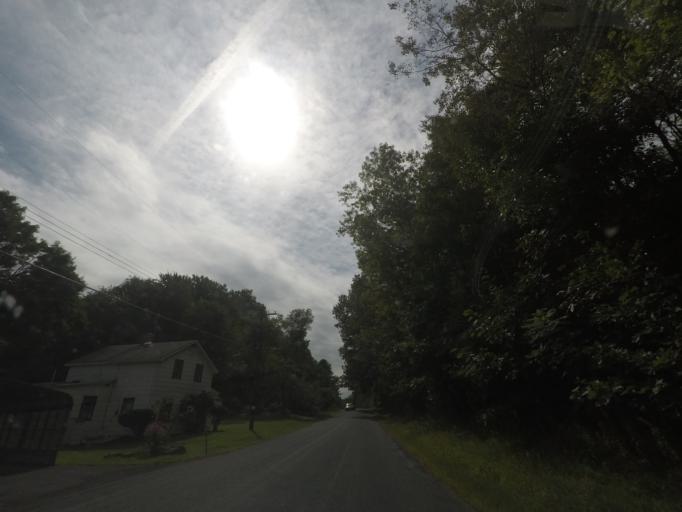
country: US
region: New York
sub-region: Rensselaer County
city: Nassau
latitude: 42.5694
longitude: -73.6108
